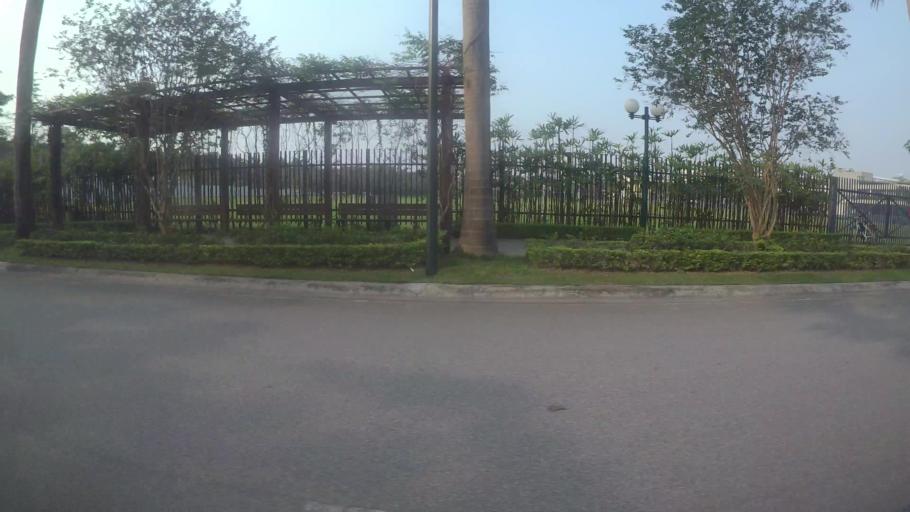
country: VN
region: Ha Noi
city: Tay Ho
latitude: 21.0749
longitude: 105.8057
